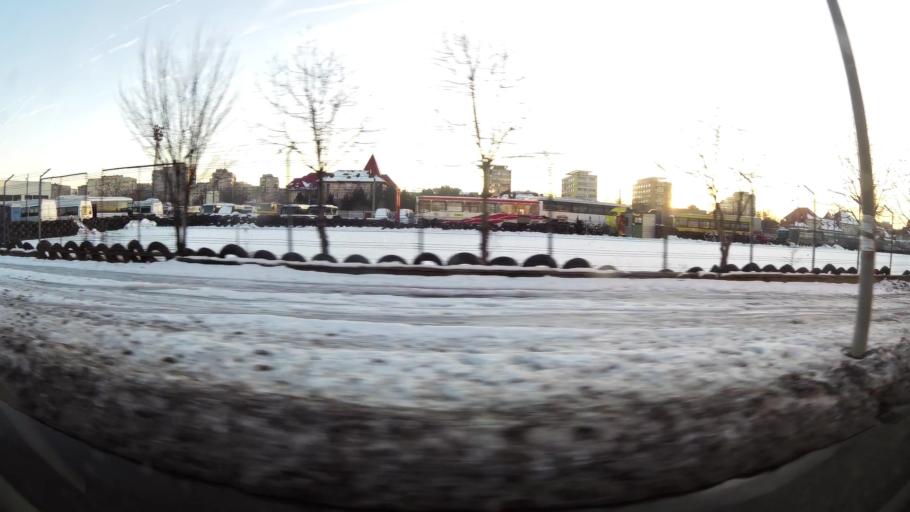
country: RO
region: Ilfov
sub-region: Comuna Fundeni-Dobroesti
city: Fundeni
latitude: 44.4490
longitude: 26.1436
